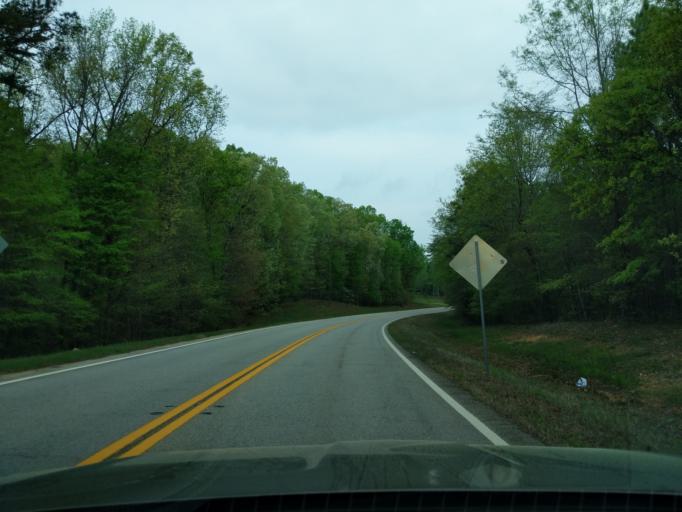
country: US
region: Georgia
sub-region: Lincoln County
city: Lincolnton
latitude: 33.7745
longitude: -82.3772
